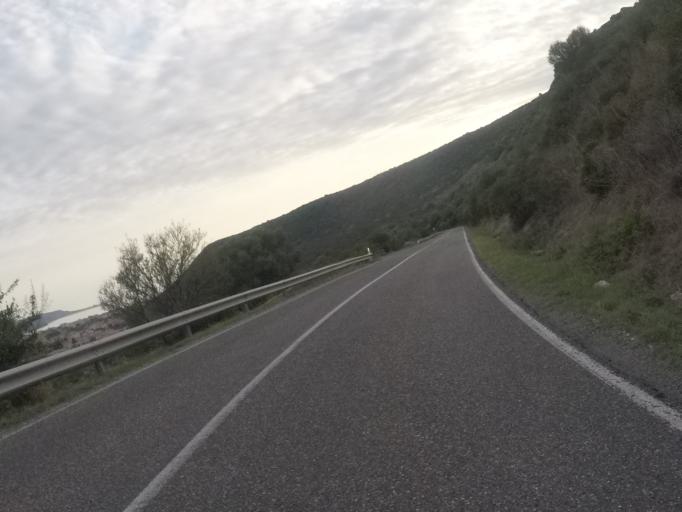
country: IT
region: Sardinia
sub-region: Provincia di Oristano
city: Bosa
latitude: 40.3107
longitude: 8.4885
